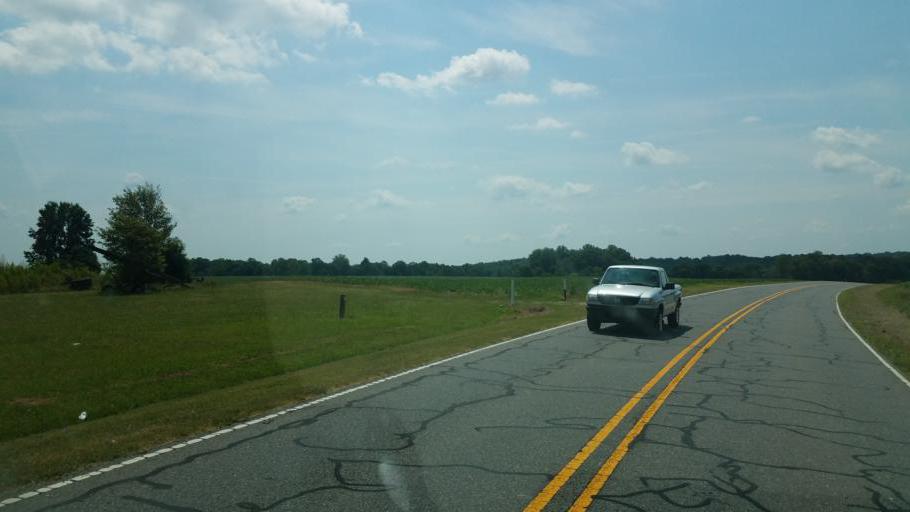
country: US
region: North Carolina
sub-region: Gaston County
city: Cherryville
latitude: 35.4277
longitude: -81.4126
